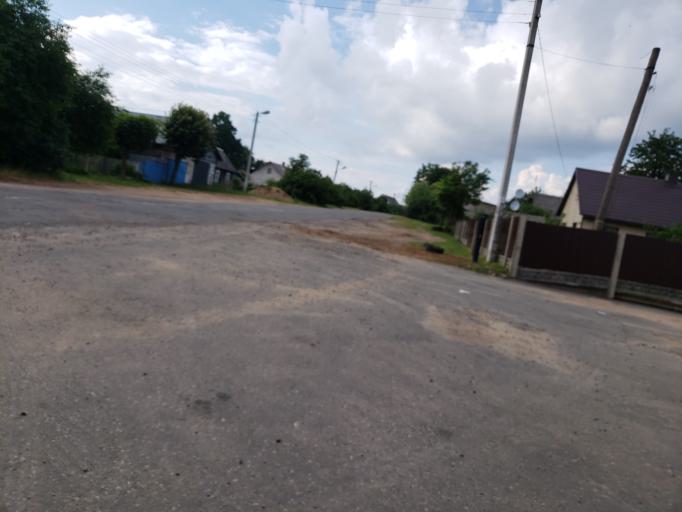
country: BY
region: Minsk
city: Chervyen'
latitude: 53.7351
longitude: 28.3883
